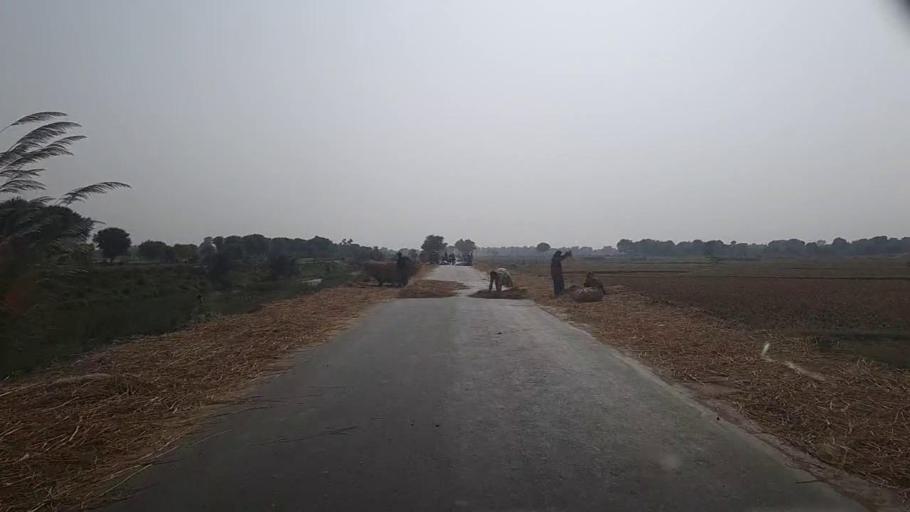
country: PK
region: Sindh
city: Kashmor
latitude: 28.4176
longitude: 69.5690
